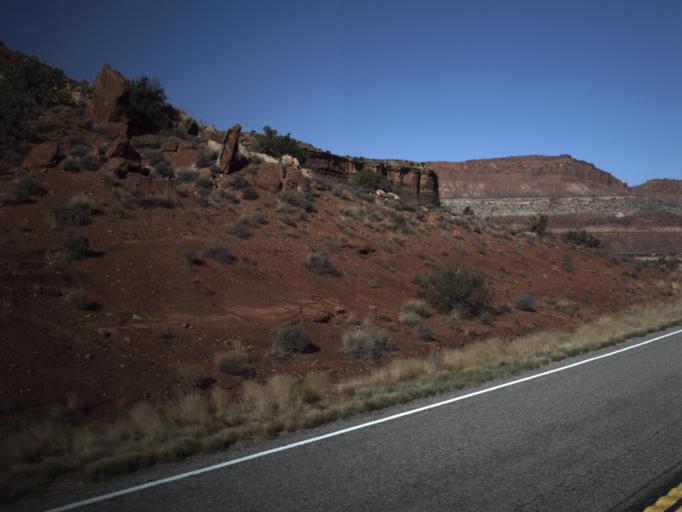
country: US
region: Utah
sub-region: San Juan County
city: Blanding
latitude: 37.7294
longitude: -110.2501
